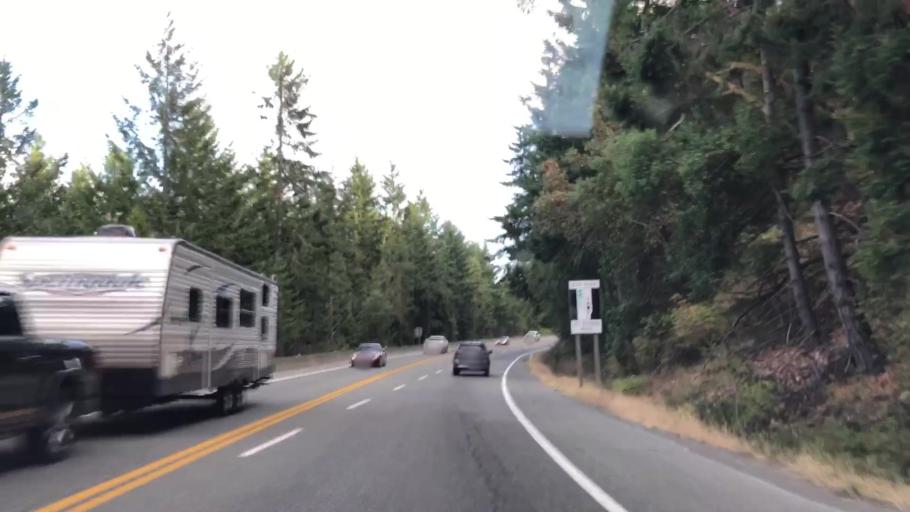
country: CA
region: British Columbia
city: Langford
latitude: 48.5756
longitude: -123.5269
